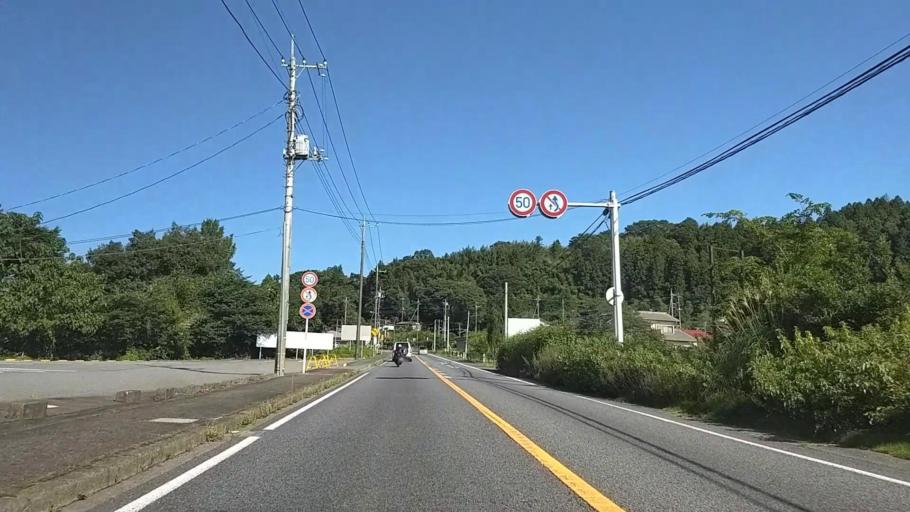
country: JP
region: Gunma
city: Annaka
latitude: 36.3231
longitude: 138.7675
